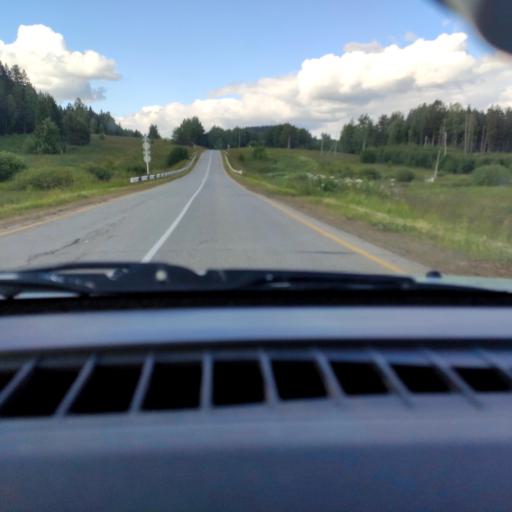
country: RU
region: Perm
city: Kukushtan
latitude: 57.3045
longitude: 56.5389
